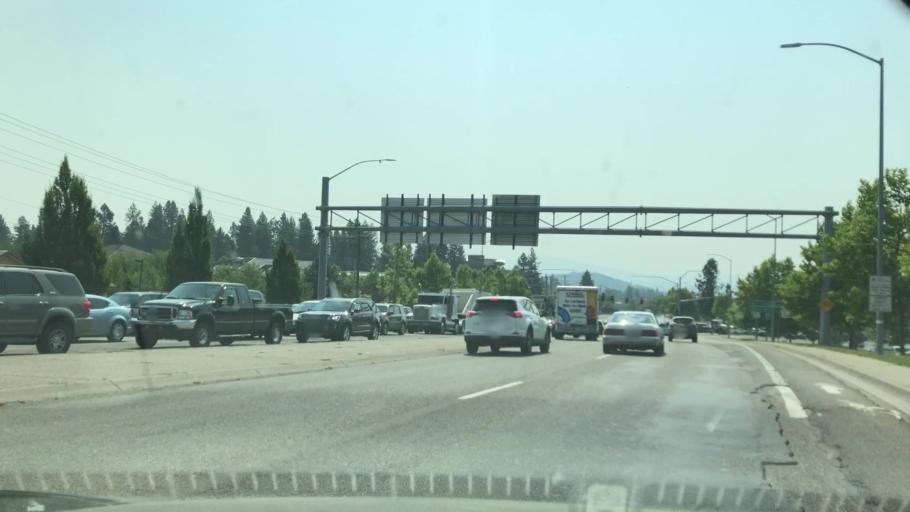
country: US
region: Idaho
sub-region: Kootenai County
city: Coeur d'Alene
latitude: 47.6988
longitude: -116.8073
